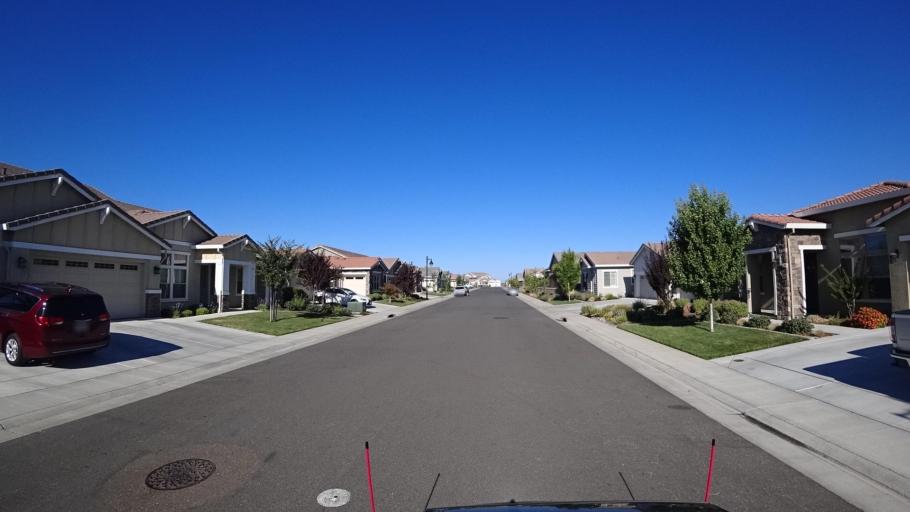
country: US
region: California
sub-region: Placer County
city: Rocklin
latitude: 38.8255
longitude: -121.2711
